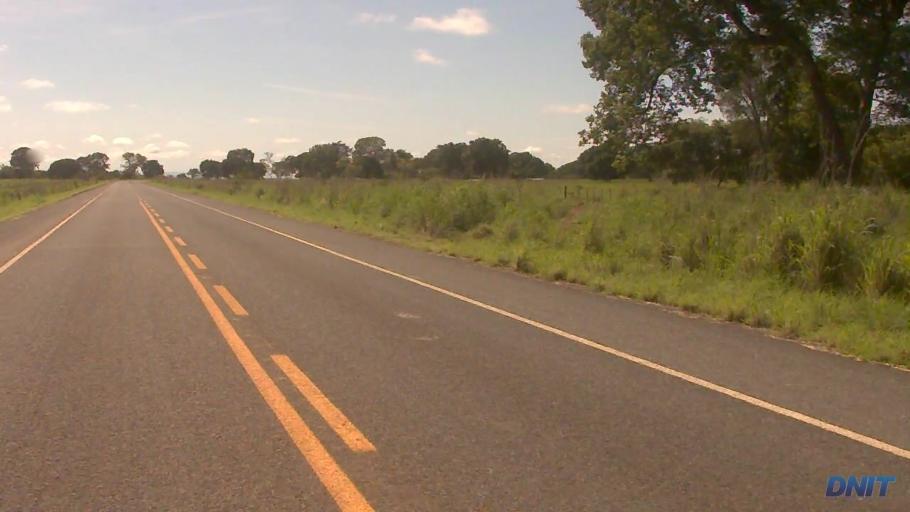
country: BR
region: Goias
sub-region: Sao Miguel Do Araguaia
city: Sao Miguel do Araguaia
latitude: -13.3173
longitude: -50.1656
